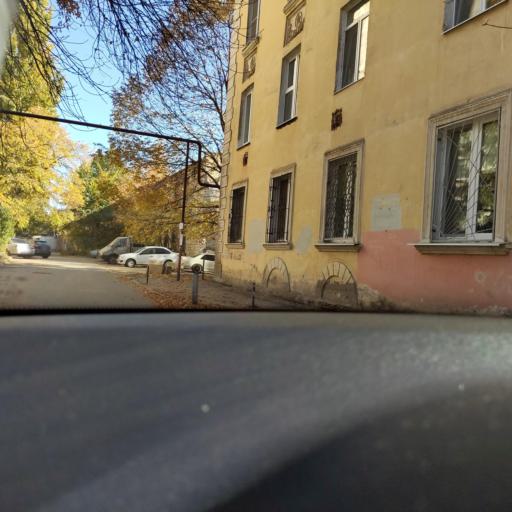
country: RU
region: Samara
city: Petra-Dubrava
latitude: 53.2320
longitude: 50.2708
